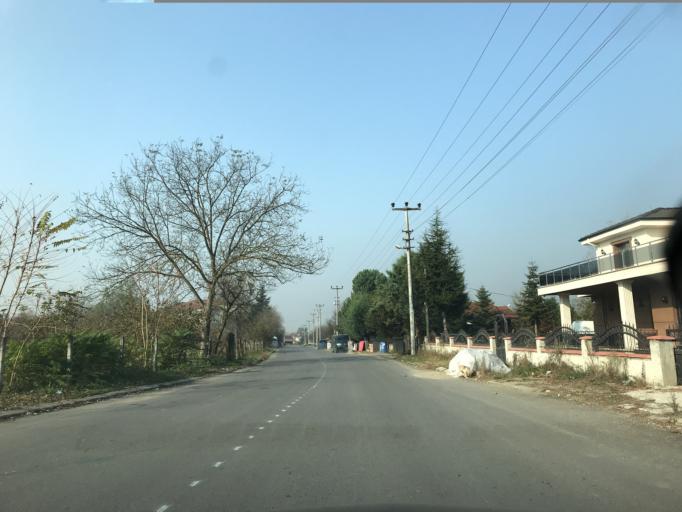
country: TR
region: Duzce
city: Duzce
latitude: 40.7897
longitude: 31.1297
